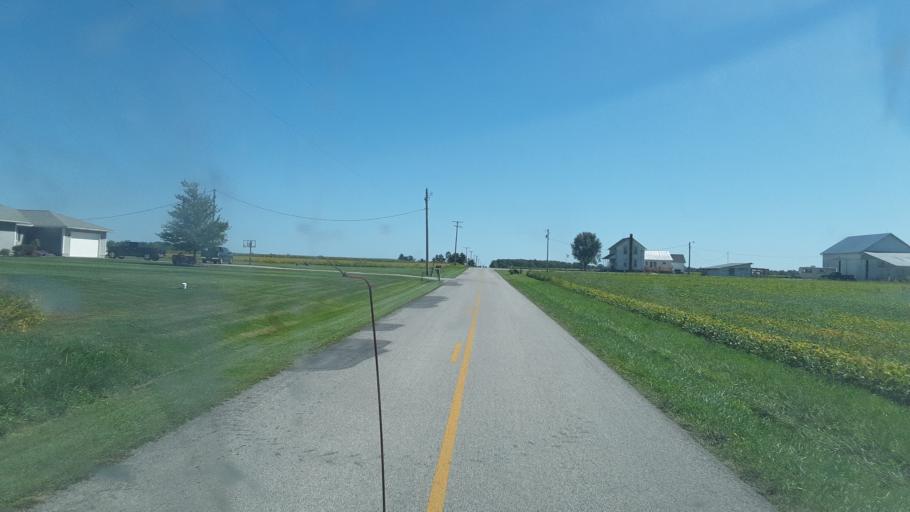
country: US
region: Ohio
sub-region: Sandusky County
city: Mount Carmel
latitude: 41.1608
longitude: -82.9074
